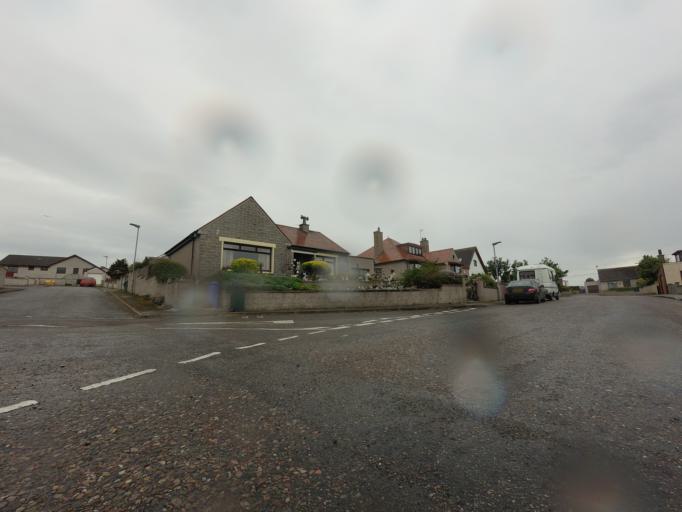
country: GB
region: Scotland
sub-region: Moray
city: Findochty
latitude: 57.6974
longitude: -2.8988
